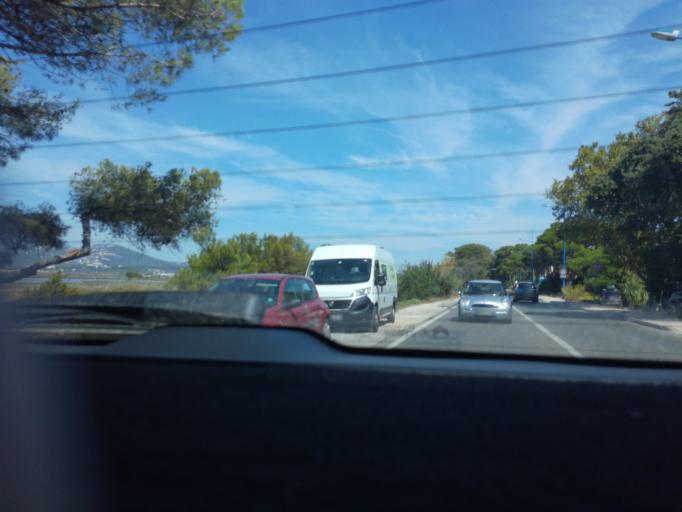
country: FR
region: Provence-Alpes-Cote d'Azur
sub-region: Departement du Var
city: Hyeres
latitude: 43.0593
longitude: 6.1470
